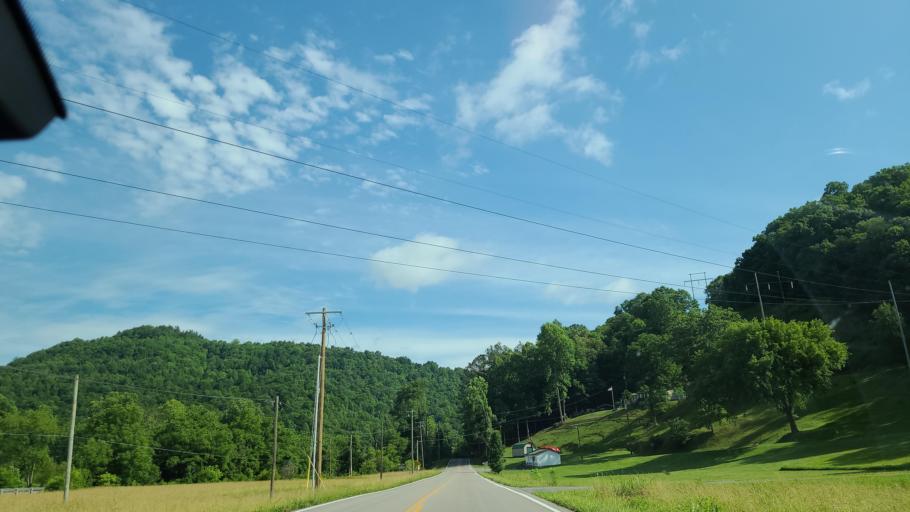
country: US
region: Kentucky
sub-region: Bell County
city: Pineville
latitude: 36.7549
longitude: -83.7815
